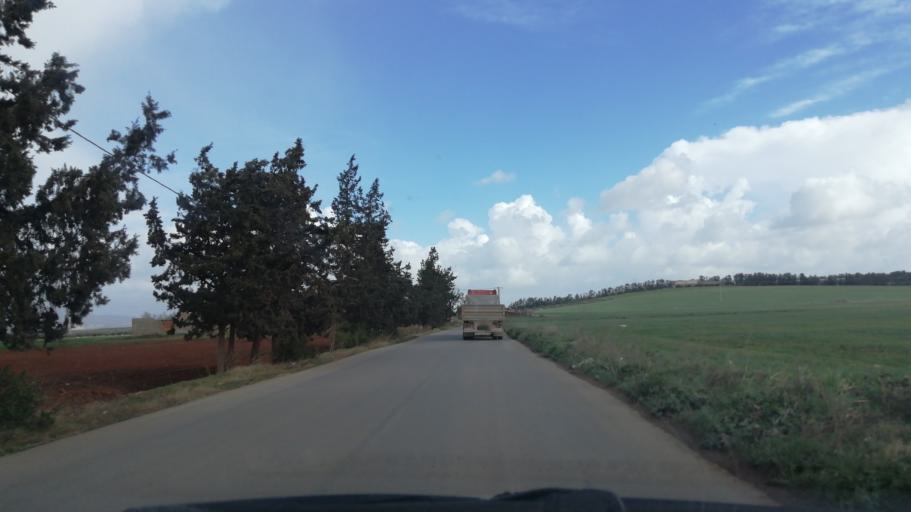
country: DZ
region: Oran
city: Sidi ech Chahmi
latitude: 35.6407
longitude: -0.5178
